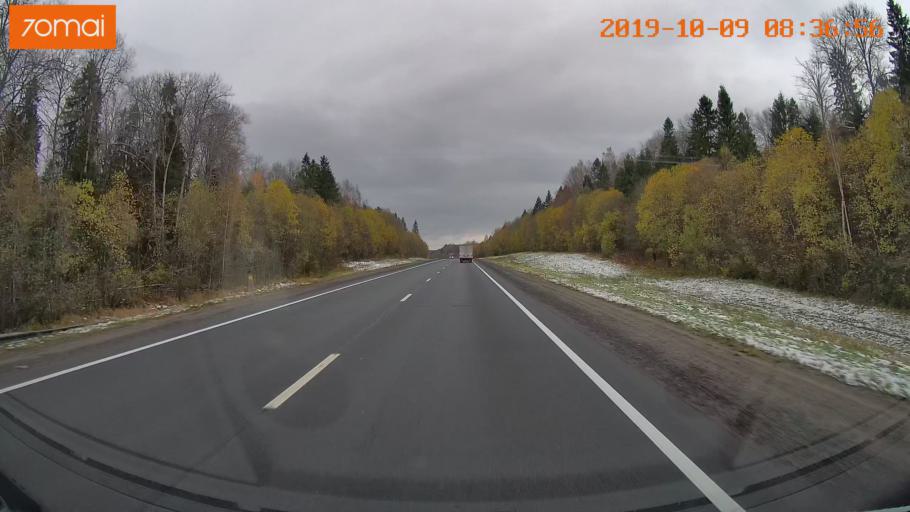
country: RU
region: Vologda
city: Gryazovets
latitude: 58.9338
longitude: 40.1757
